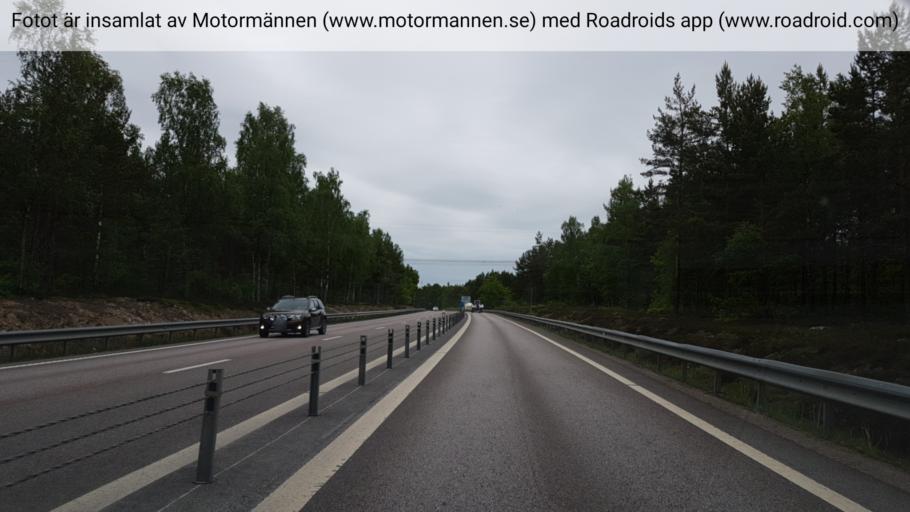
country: SE
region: Kalmar
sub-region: Oskarshamns Kommun
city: Oskarshamn
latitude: 57.3939
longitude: 16.4780
